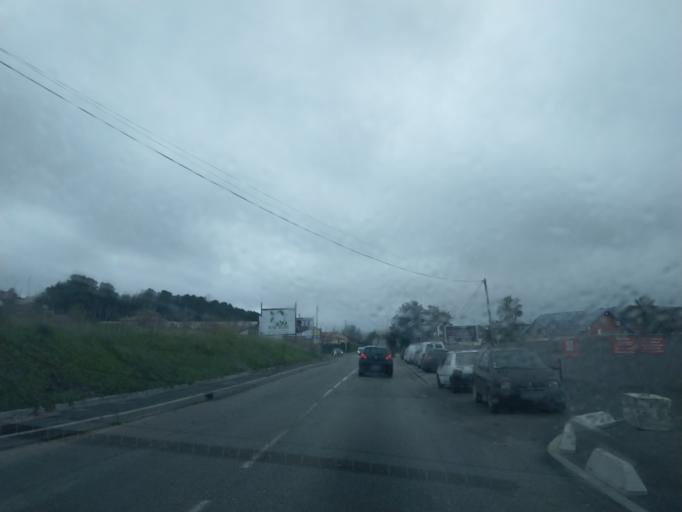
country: FR
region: Provence-Alpes-Cote d'Azur
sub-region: Departement des Bouches-du-Rhone
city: Septemes-les-Vallons
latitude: 43.4142
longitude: 5.3669
